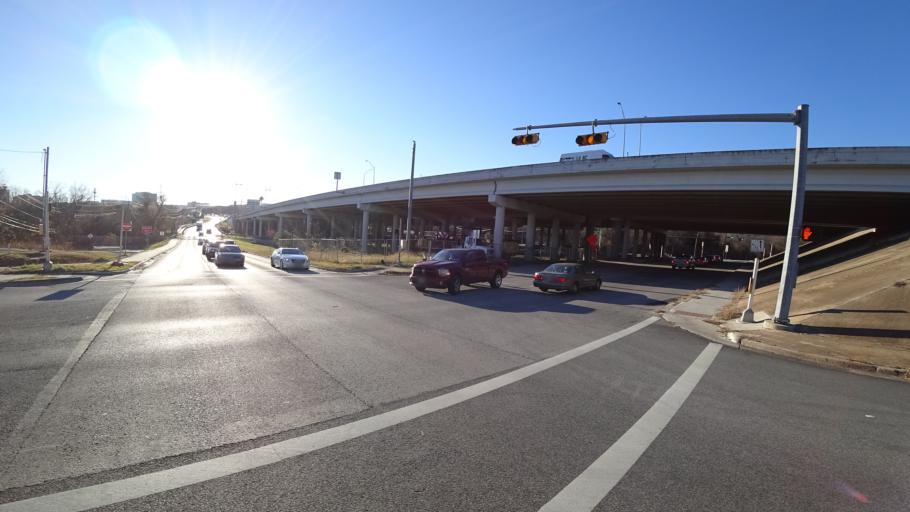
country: US
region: Texas
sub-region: Travis County
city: Wells Branch
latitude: 30.4108
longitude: -97.7095
